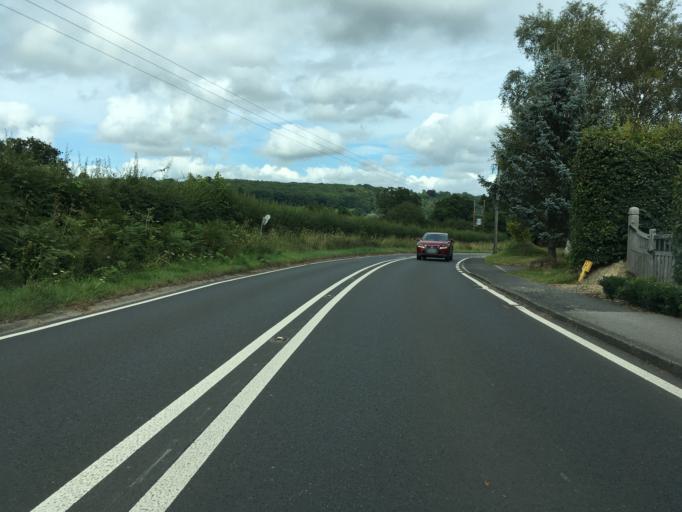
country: GB
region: England
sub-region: East Sussex
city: Crowborough
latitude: 51.1122
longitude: 0.1792
